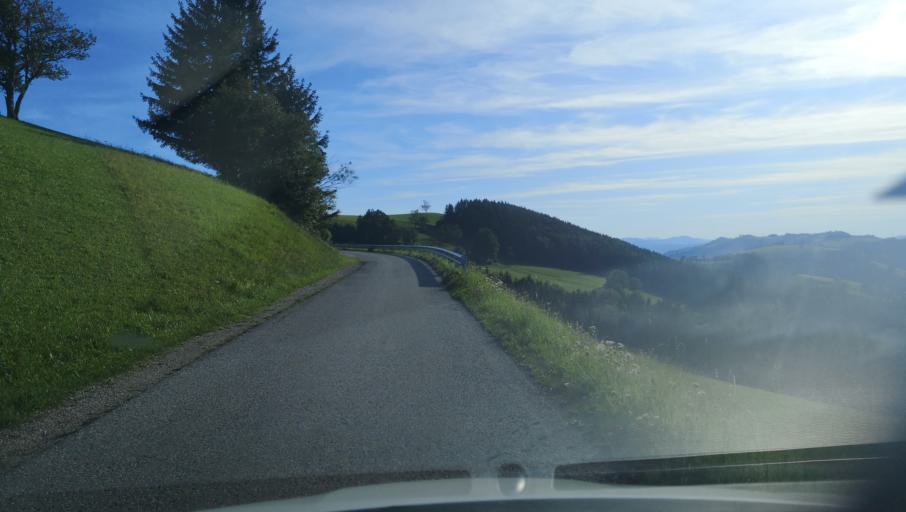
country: AT
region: Lower Austria
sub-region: Politischer Bezirk Amstetten
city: Neuhofen an der Ybbs
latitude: 48.0121
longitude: 14.8907
